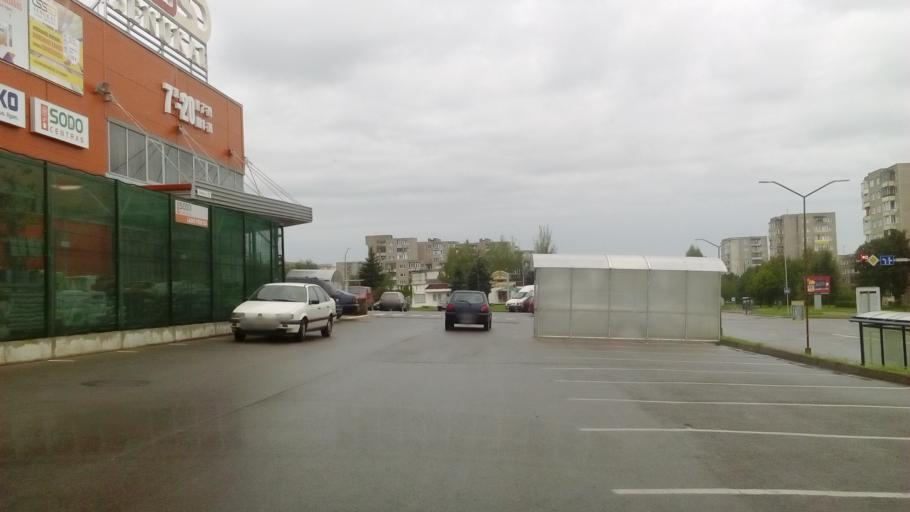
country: LT
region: Alytaus apskritis
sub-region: Alytus
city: Alytus
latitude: 54.3930
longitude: 24.0185
